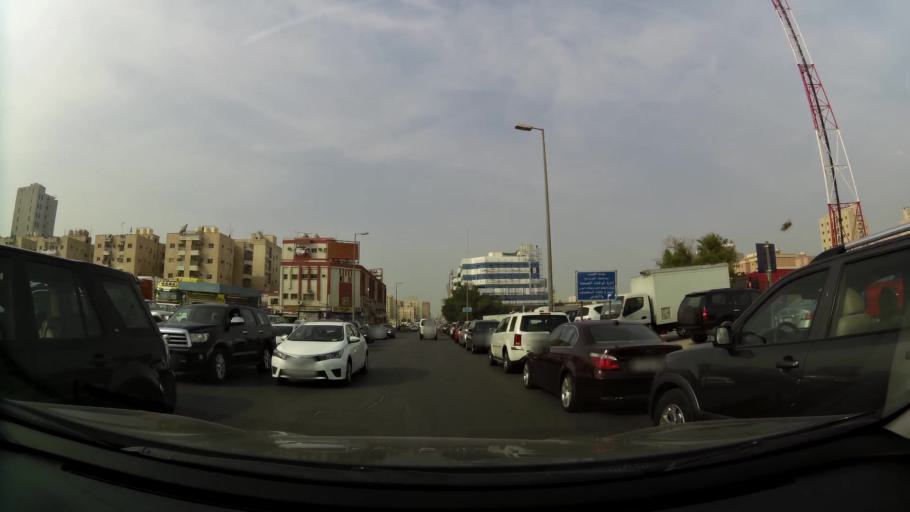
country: KW
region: Al Farwaniyah
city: Janub as Surrah
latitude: 29.2876
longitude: 47.9748
